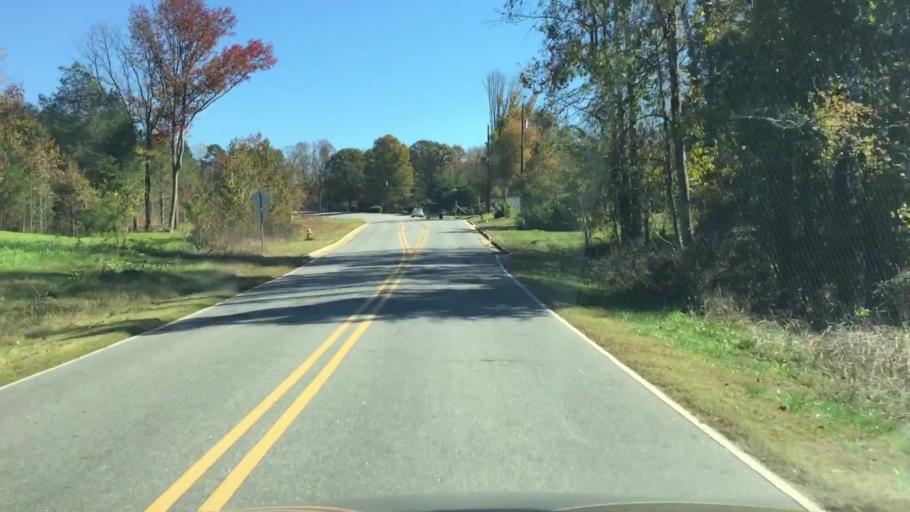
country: US
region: North Carolina
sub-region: Iredell County
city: Mooresville
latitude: 35.5451
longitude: -80.7804
